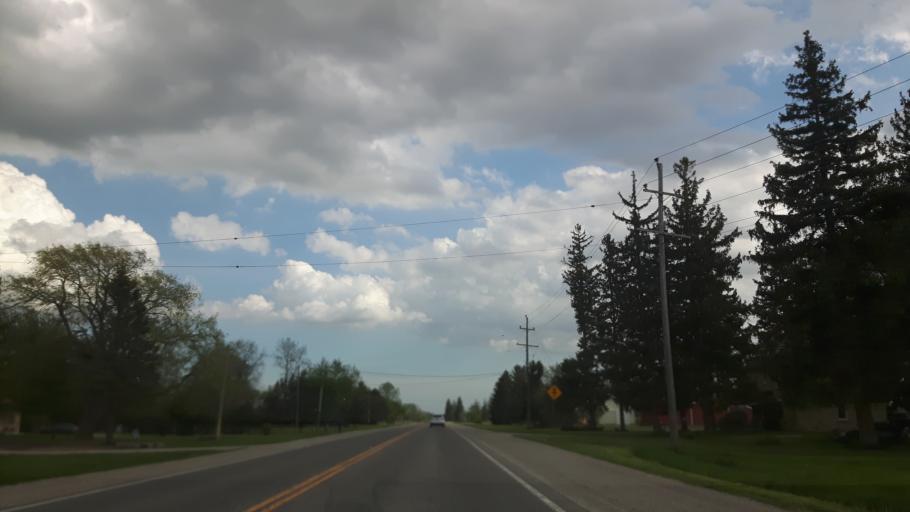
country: CA
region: Ontario
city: South Huron
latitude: 43.2368
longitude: -81.4587
